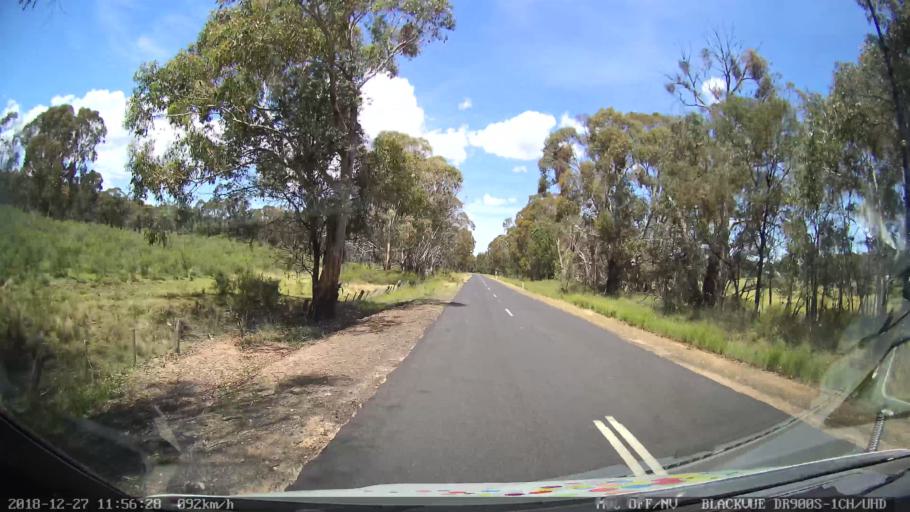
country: AU
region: New South Wales
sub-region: Blayney
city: Blayney
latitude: -33.6989
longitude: 149.3914
